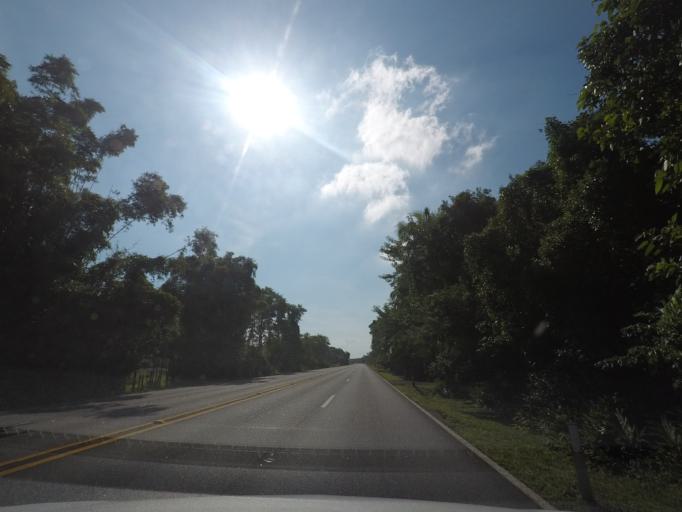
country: BR
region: Parana
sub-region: Pontal Do Parana
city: Pontal do Parana
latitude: -25.6346
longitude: -48.5936
